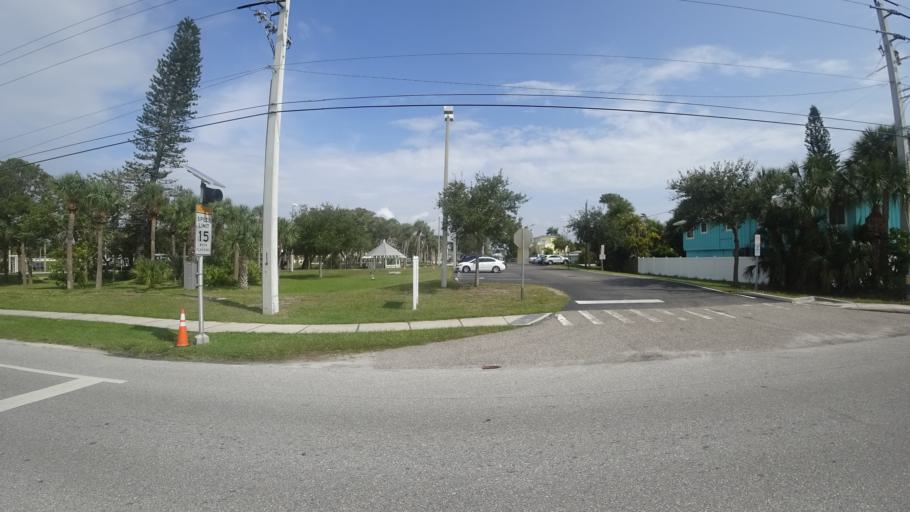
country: US
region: Florida
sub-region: Manatee County
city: Holmes Beach
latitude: 27.5020
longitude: -82.7127
